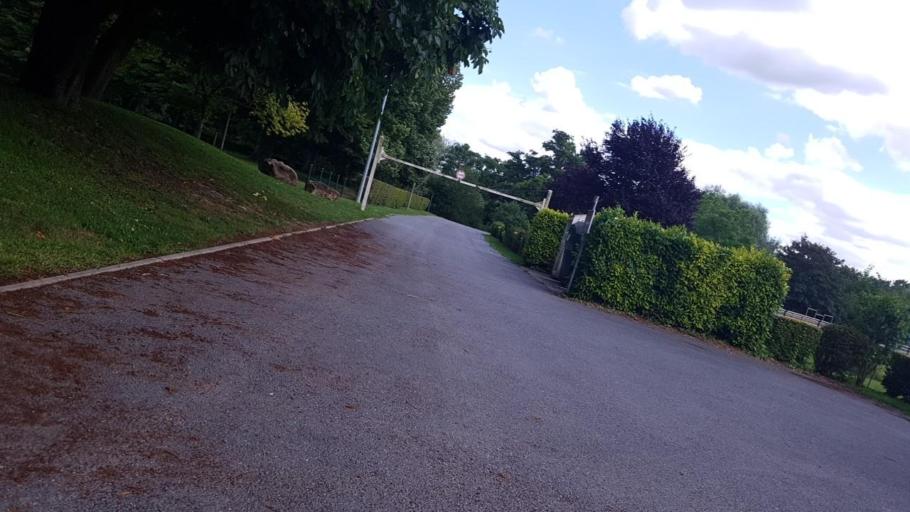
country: FR
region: Picardie
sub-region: Departement de l'Aisne
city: Crezancy
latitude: 49.0866
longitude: 3.5349
